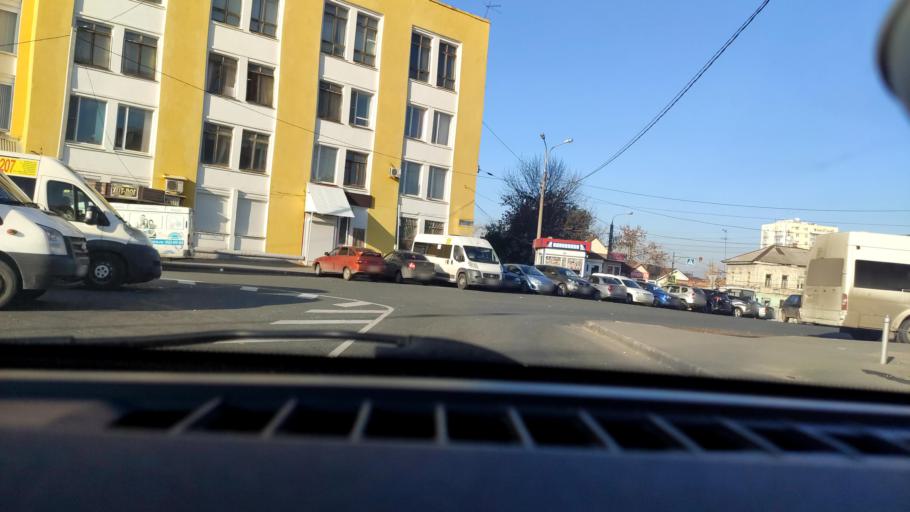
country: RU
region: Samara
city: Rozhdestveno
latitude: 53.1789
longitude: 50.0798
